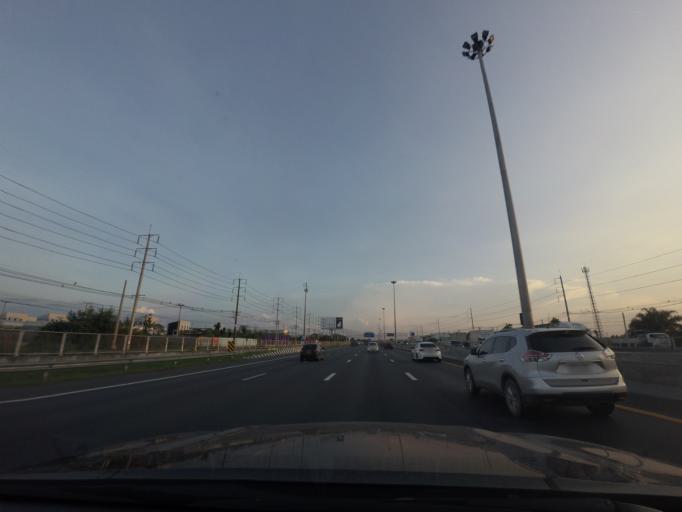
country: TH
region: Pathum Thani
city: Lam Luk Ka
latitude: 13.9546
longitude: 100.7129
